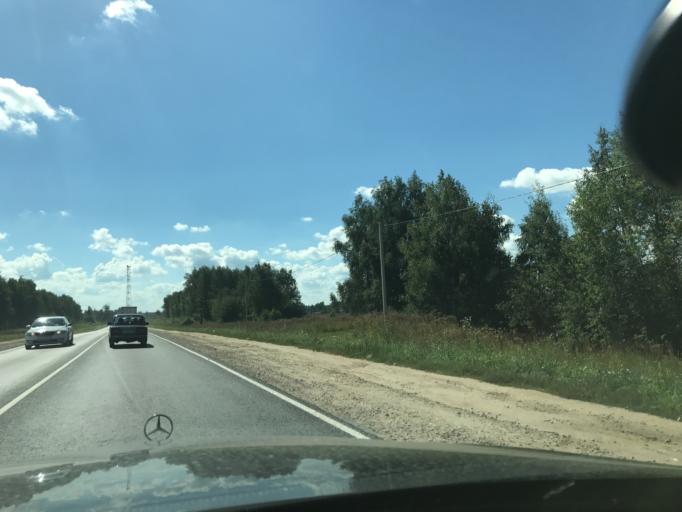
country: RU
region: Vladimir
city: Vorsha
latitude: 56.0657
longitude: 40.1193
